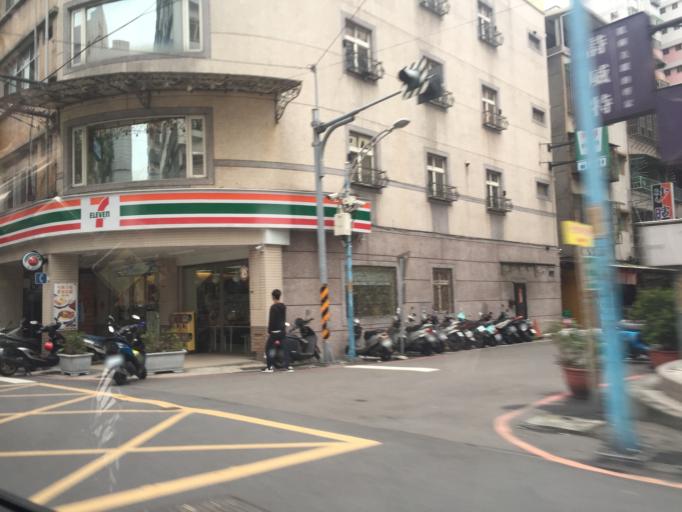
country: TW
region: Taiwan
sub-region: Taoyuan
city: Taoyuan
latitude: 24.9304
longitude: 121.3721
